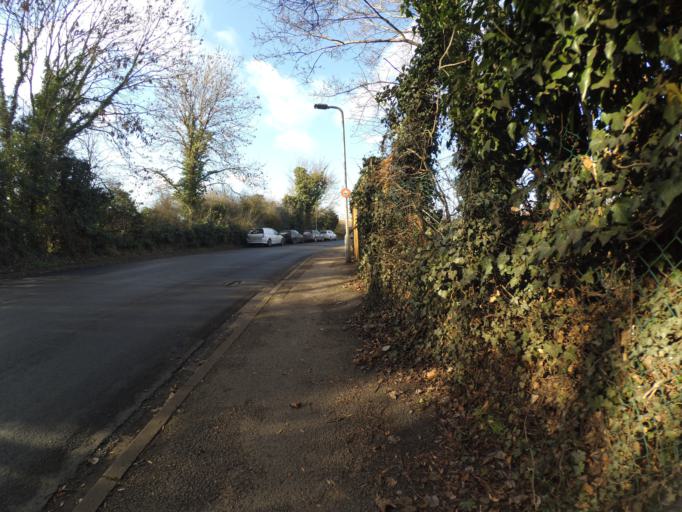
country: GB
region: England
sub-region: Derbyshire
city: Long Eaton
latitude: 52.9170
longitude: -1.2237
